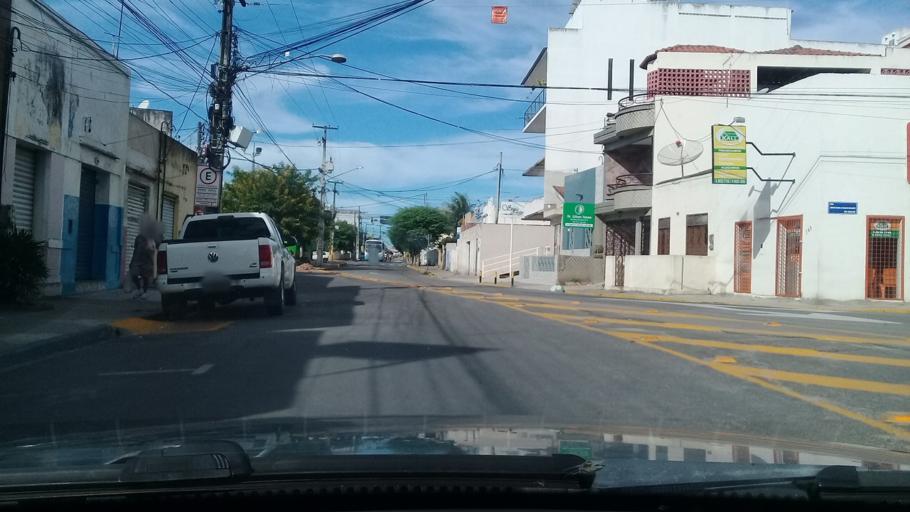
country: BR
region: Pernambuco
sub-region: Vitoria De Santo Antao
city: Vitoria de Santo Antao
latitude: -8.1152
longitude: -35.2933
